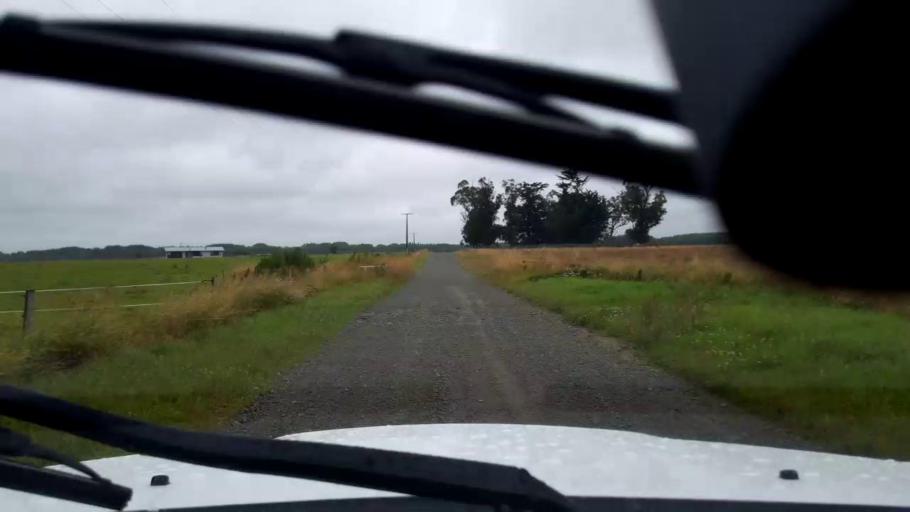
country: NZ
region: Canterbury
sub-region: Timaru District
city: Pleasant Point
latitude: -44.2491
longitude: 171.2006
